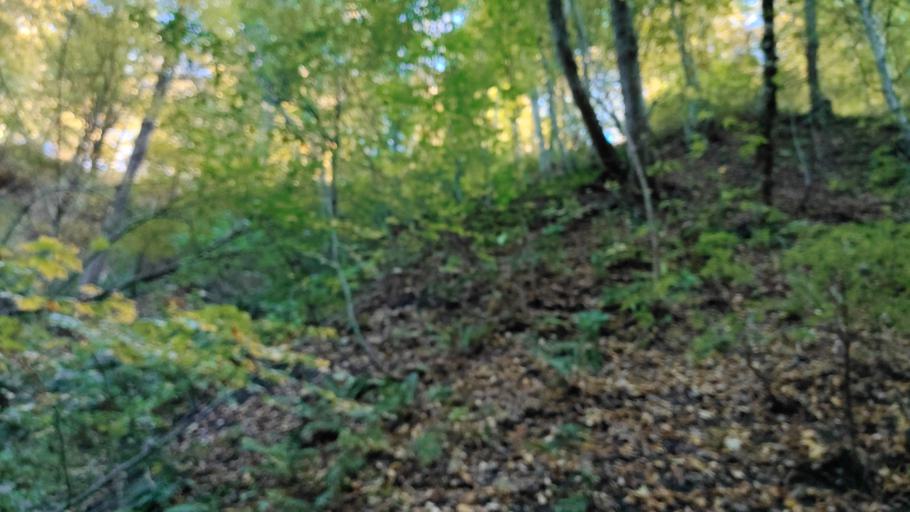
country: RU
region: Krasnodarskiy
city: Goryachiy Klyuch
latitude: 44.5931
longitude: 39.1240
